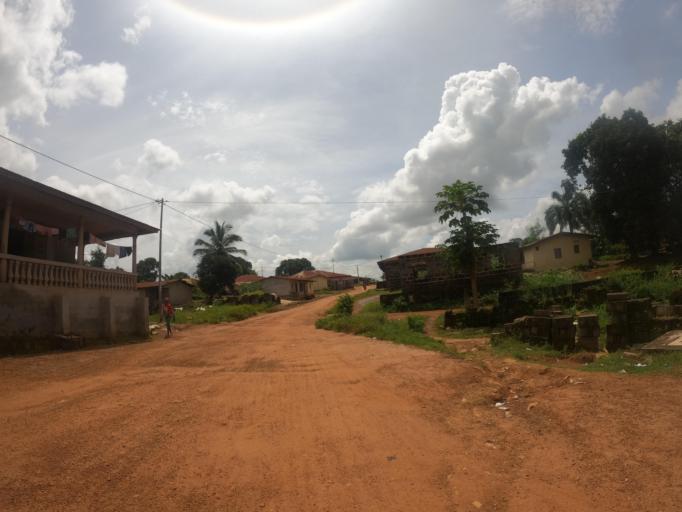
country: SL
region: Northern Province
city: Makeni
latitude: 8.8953
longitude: -12.0500
